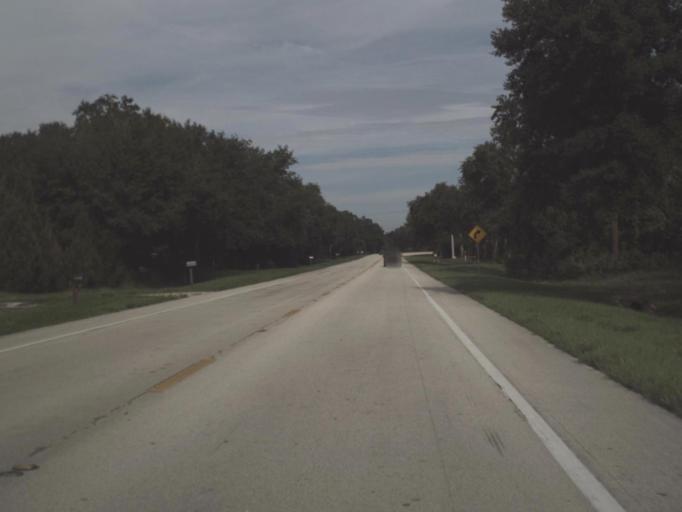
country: US
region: Florida
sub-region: DeSoto County
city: Southeast Arcadia
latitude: 27.1690
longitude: -81.8245
